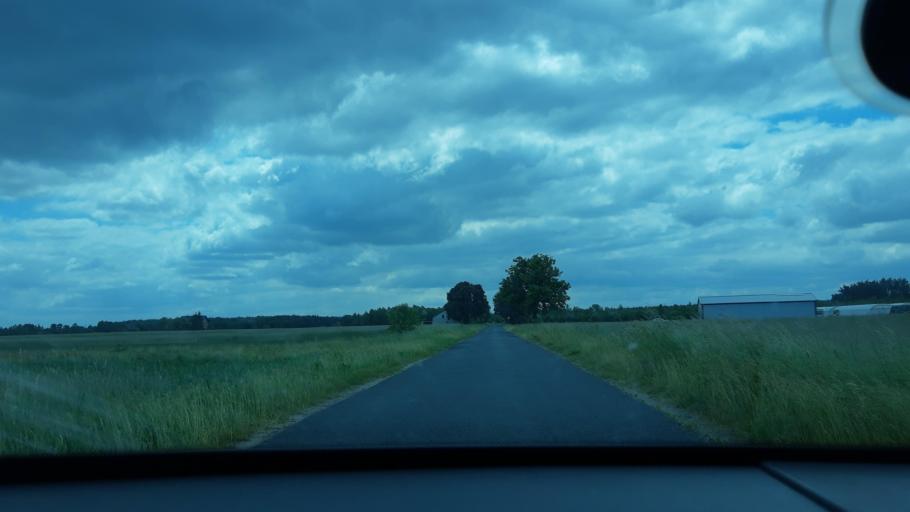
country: PL
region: Lodz Voivodeship
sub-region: Powiat zdunskowolski
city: Zapolice
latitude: 51.5092
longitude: 18.8466
